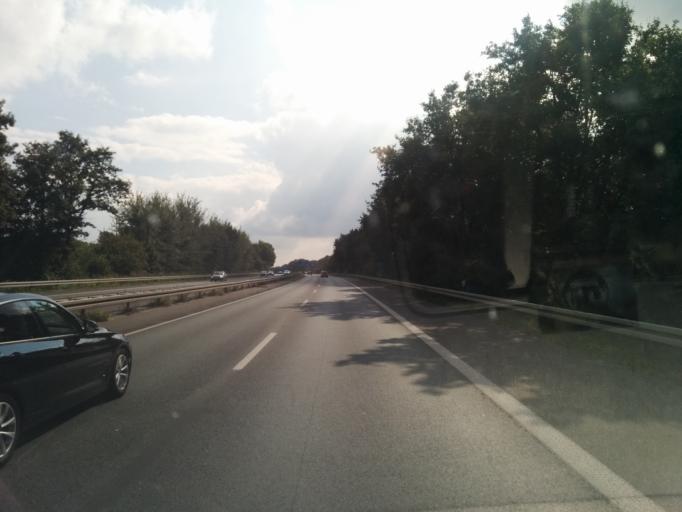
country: DE
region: North Rhine-Westphalia
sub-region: Regierungsbezirk Munster
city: Recklinghausen
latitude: 51.6294
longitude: 7.1666
